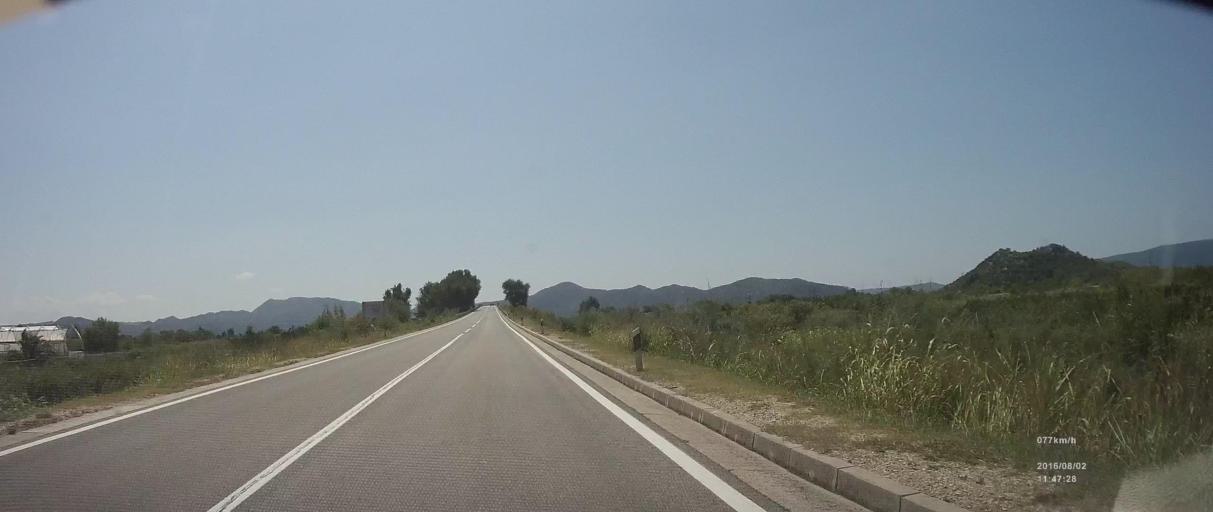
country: HR
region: Dubrovacko-Neretvanska
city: Komin
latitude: 43.0435
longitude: 17.4823
